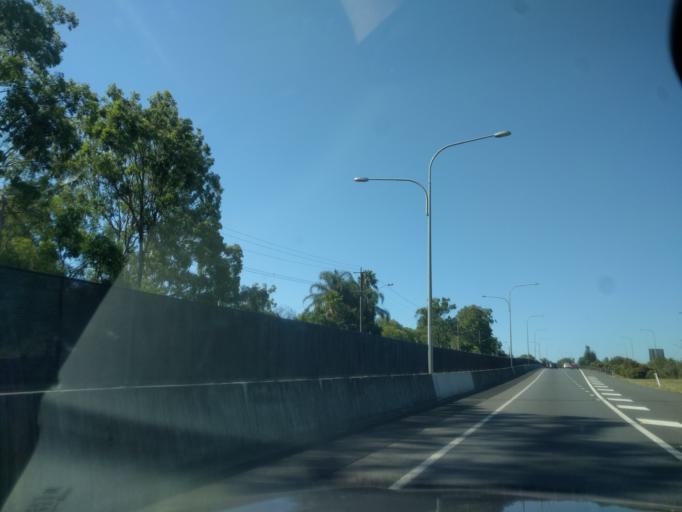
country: AU
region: Queensland
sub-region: Logan
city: Park Ridge South
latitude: -27.7174
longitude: 153.0327
